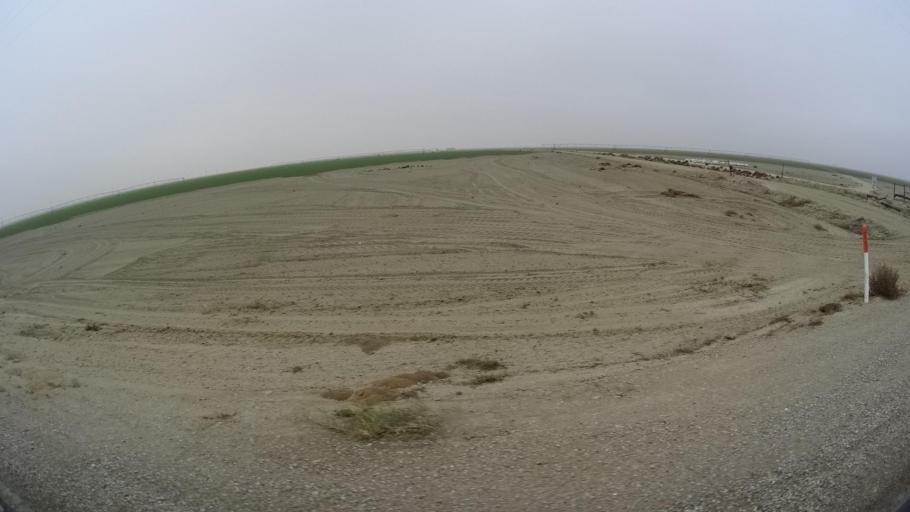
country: US
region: California
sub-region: Kern County
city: Maricopa
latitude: 35.1565
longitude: -119.1990
